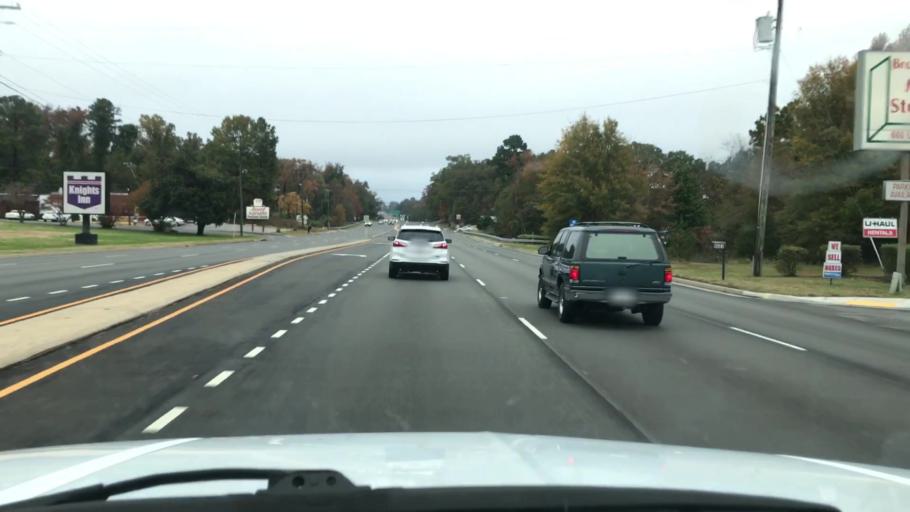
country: US
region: Virginia
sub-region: Henrico County
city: Chamberlayne
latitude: 37.6455
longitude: -77.4600
